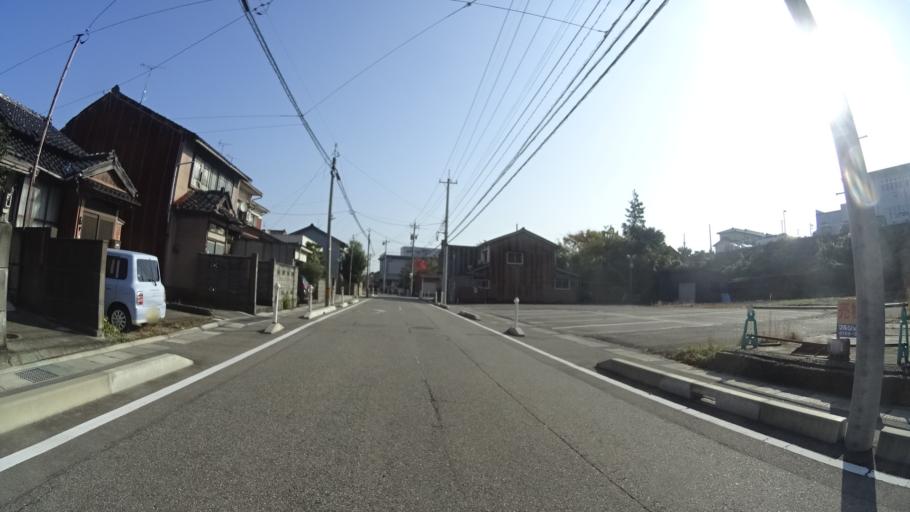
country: JP
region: Toyama
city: Nishishinminato
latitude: 36.7944
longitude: 137.0534
